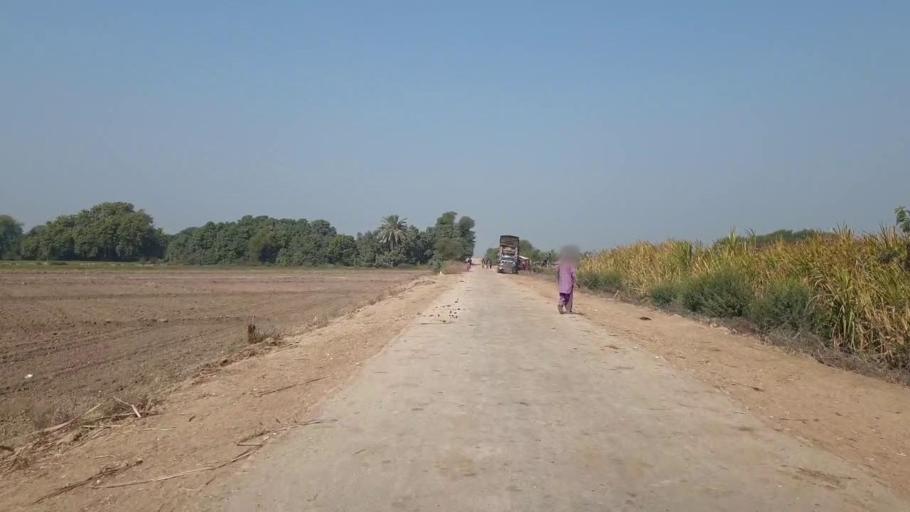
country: PK
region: Sindh
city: Bhit Shah
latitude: 25.7779
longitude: 68.5131
